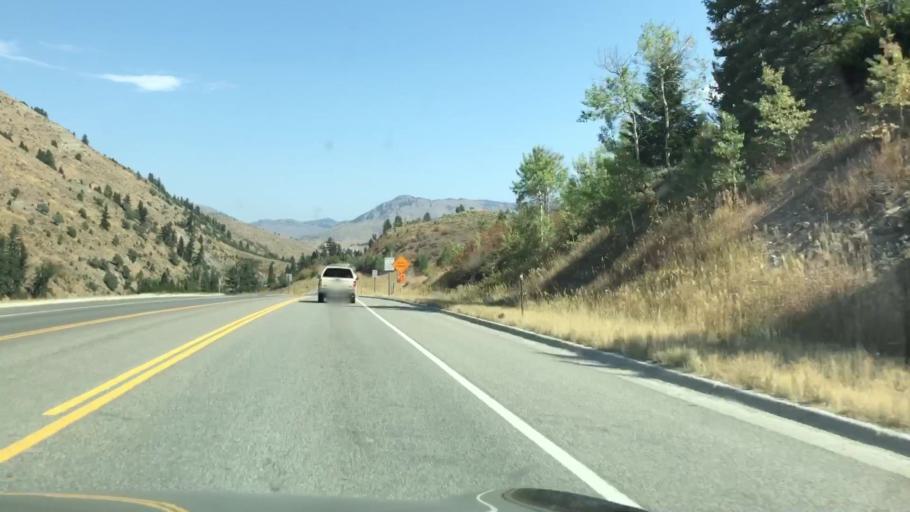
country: US
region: Wyoming
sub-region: Teton County
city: Hoback
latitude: 43.3265
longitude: -110.7293
